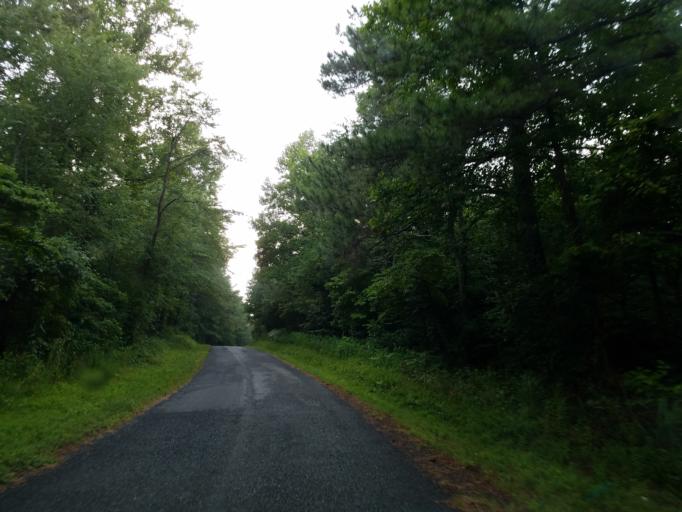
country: US
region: Georgia
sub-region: Pickens County
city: Jasper
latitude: 34.4963
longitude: -84.5236
